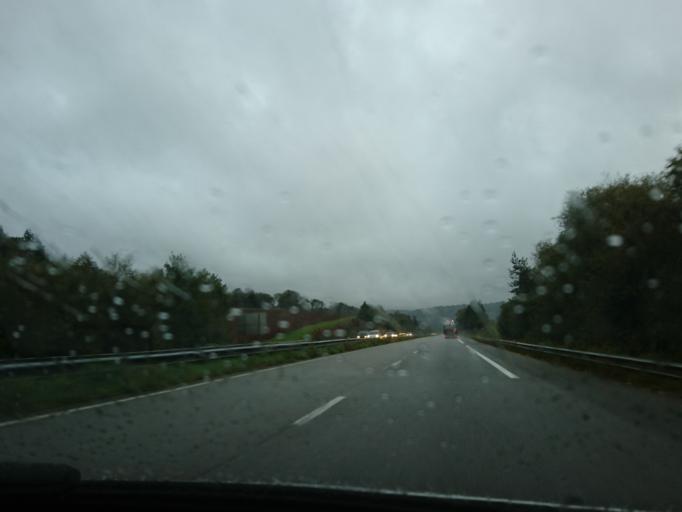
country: FR
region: Brittany
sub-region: Departement du Finistere
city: Chateaulin
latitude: 48.1989
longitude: -4.0443
